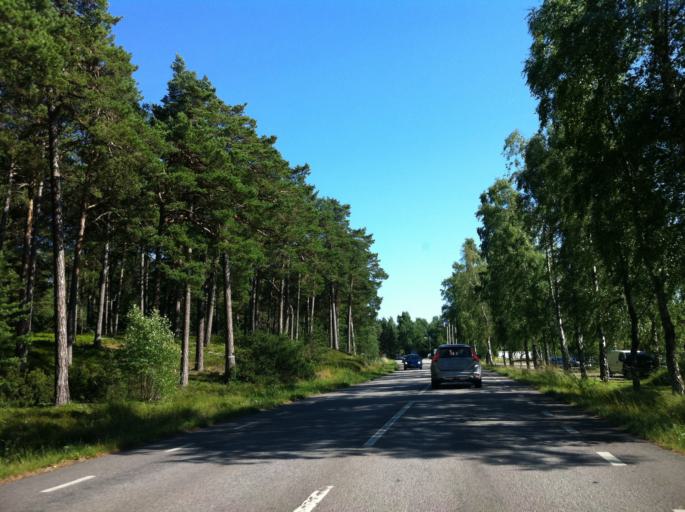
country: SE
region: Kalmar
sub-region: Borgholms Kommun
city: Borgholm
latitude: 57.2964
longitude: 17.0210
